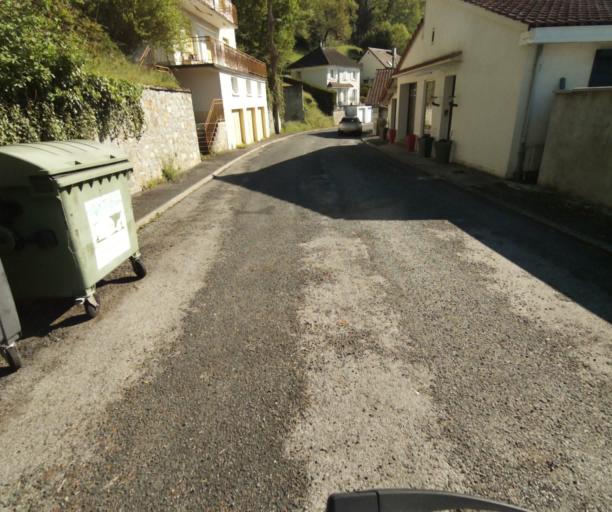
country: FR
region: Limousin
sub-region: Departement de la Correze
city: Tulle
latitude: 45.2774
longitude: 1.7734
